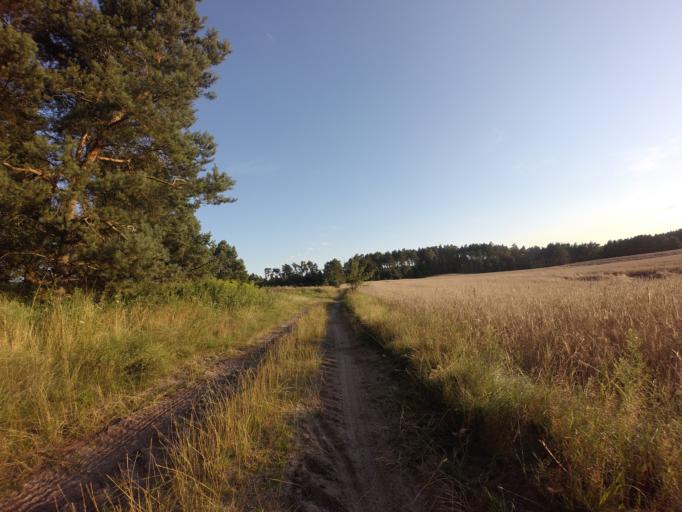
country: PL
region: West Pomeranian Voivodeship
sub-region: Powiat choszczenski
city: Choszczno
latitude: 53.2158
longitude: 15.4245
